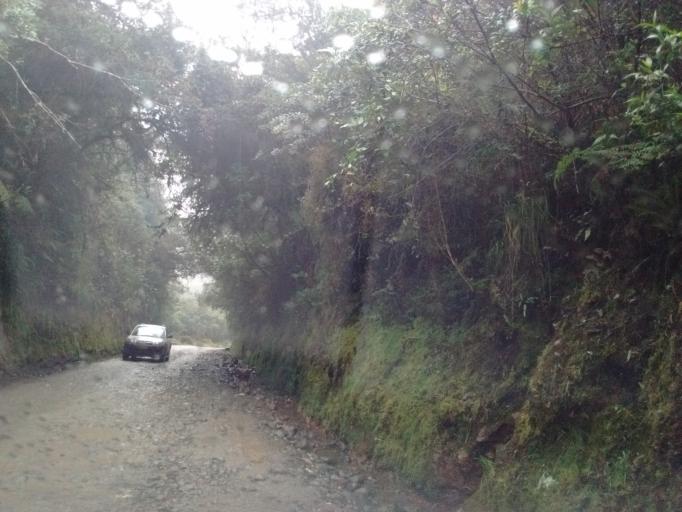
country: CO
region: Cauca
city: Paispamba
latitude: 2.1675
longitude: -76.4188
